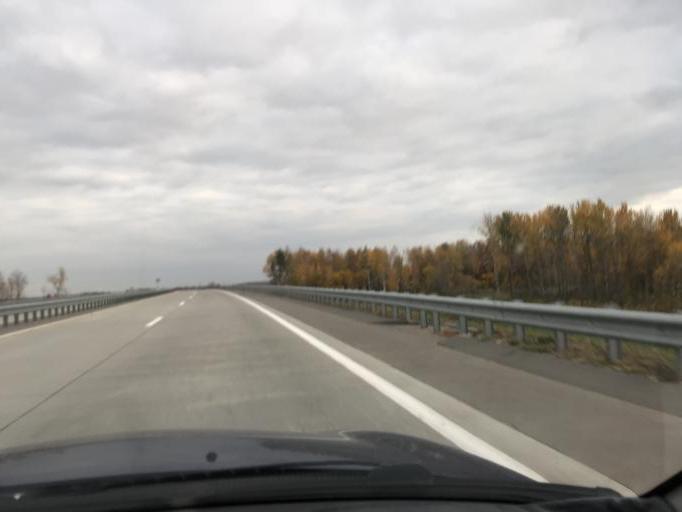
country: BY
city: Fanipol
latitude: 53.7676
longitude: 27.3671
